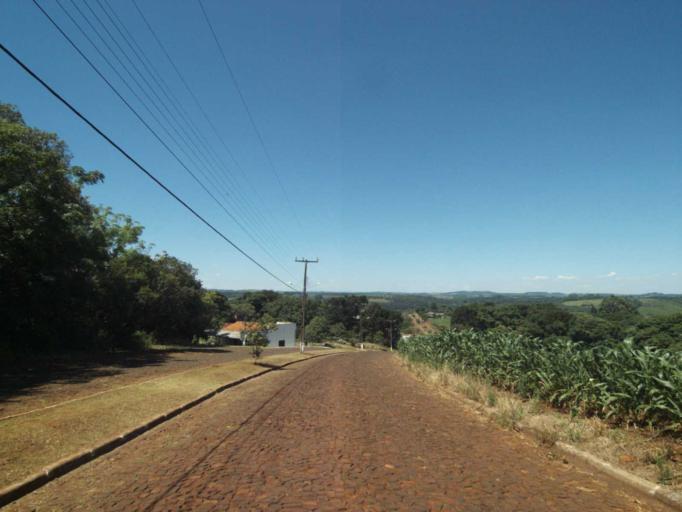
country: BR
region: Parana
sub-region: Laranjeiras Do Sul
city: Laranjeiras do Sul
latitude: -25.3879
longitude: -52.2122
